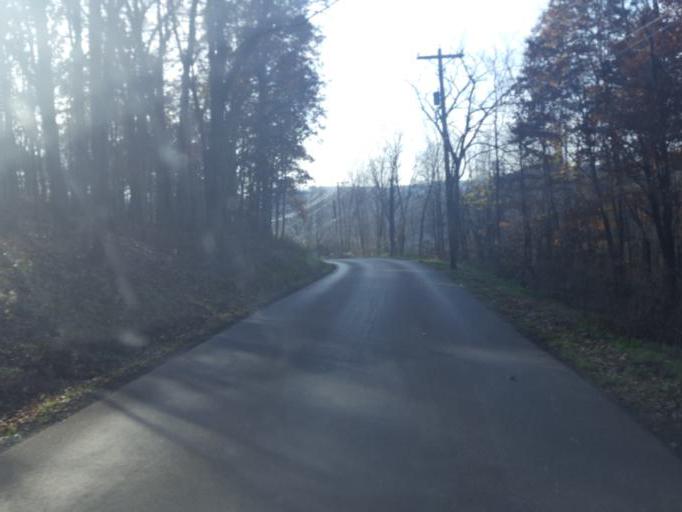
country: US
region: Ohio
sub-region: Knox County
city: Gambier
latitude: 40.3912
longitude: -82.4110
